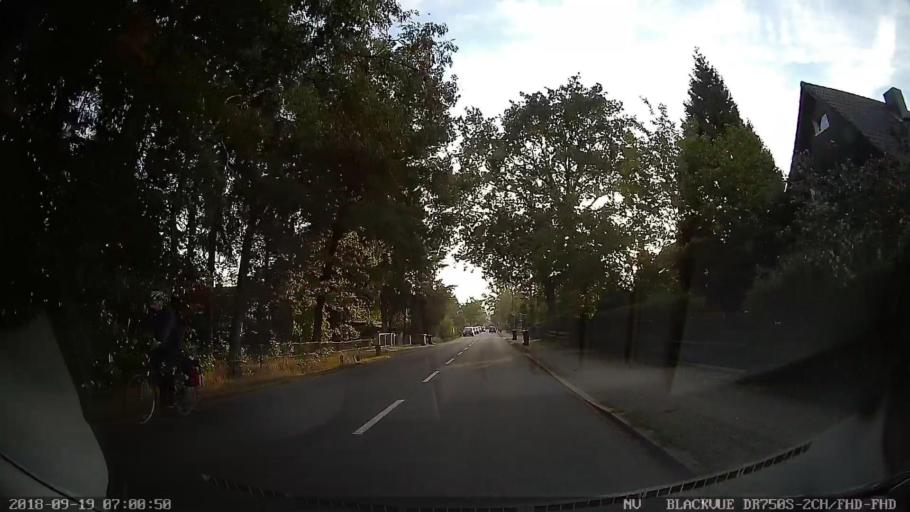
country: DE
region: Hamburg
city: Eidelstedt
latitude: 53.6312
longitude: 9.8974
